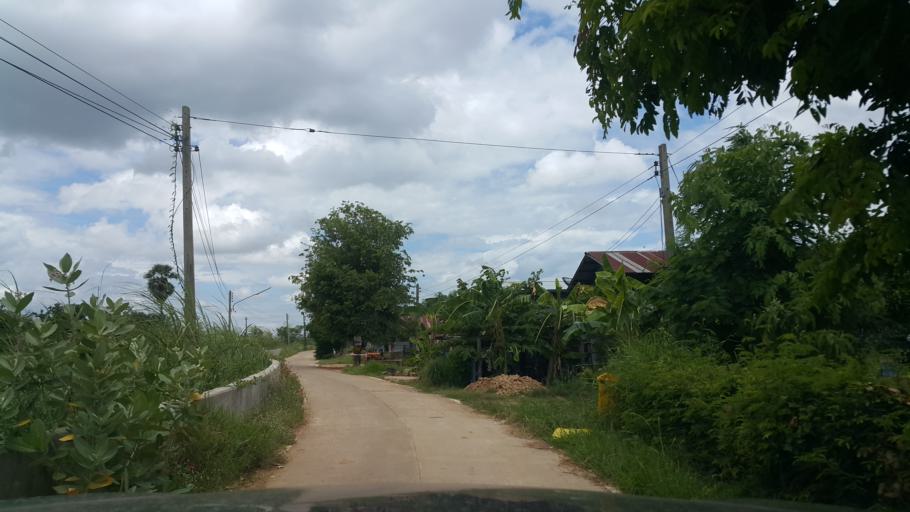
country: TH
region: Sukhothai
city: Sukhothai
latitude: 17.0225
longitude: 99.7957
